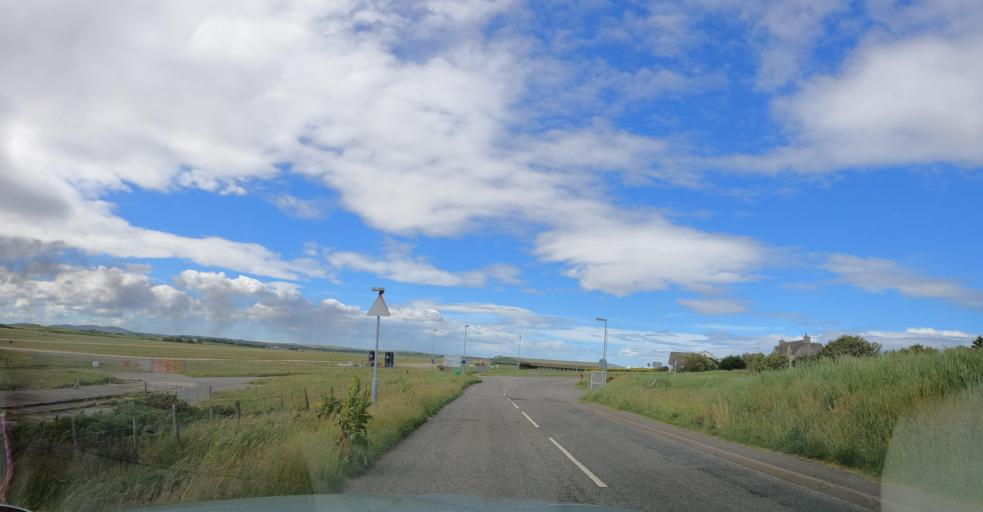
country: GB
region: Scotland
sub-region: Eilean Siar
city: Stornoway
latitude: 58.2090
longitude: -6.3230
